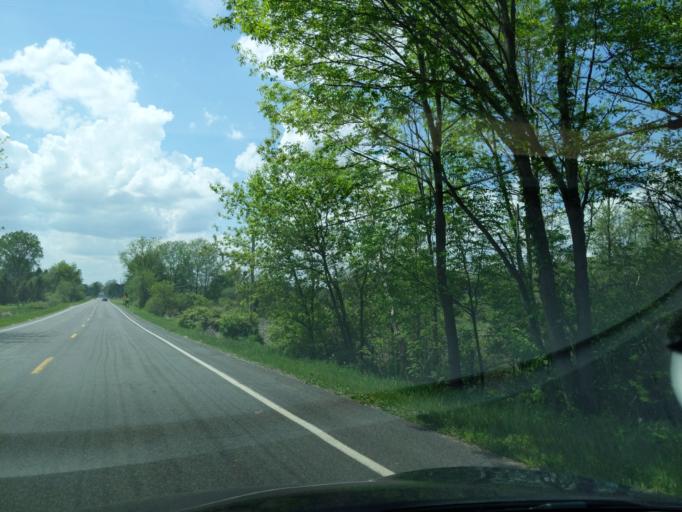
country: US
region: Michigan
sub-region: Ingham County
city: Mason
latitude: 42.5965
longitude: -84.3992
